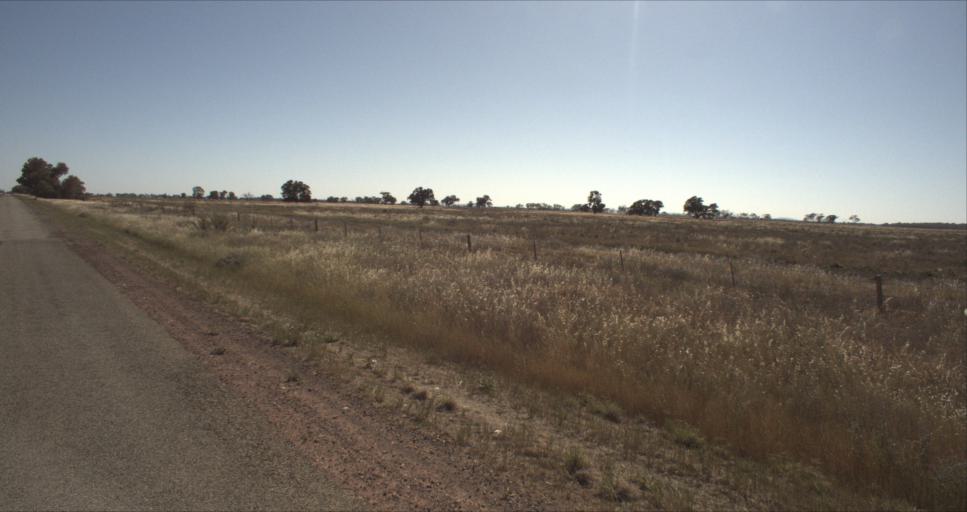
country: AU
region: New South Wales
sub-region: Leeton
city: Leeton
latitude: -34.6016
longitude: 146.2576
